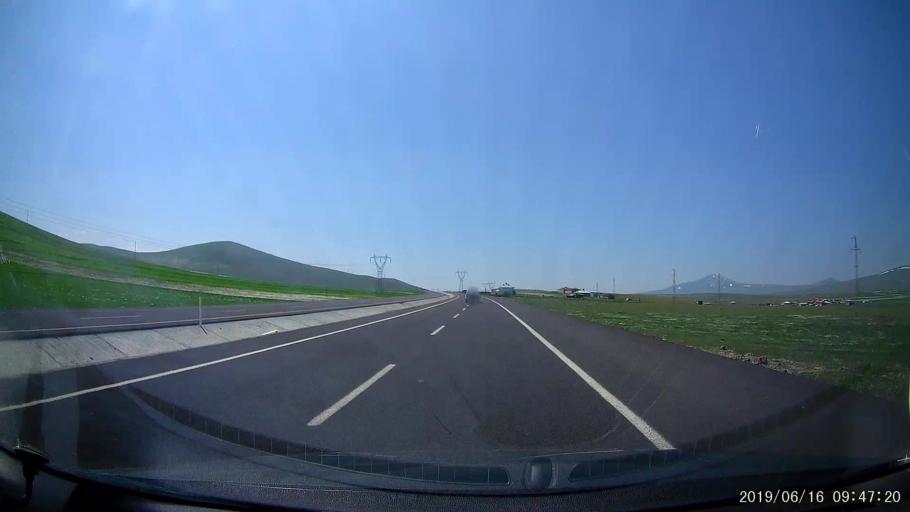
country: TR
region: Kars
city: Digor
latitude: 40.4495
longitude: 43.3426
